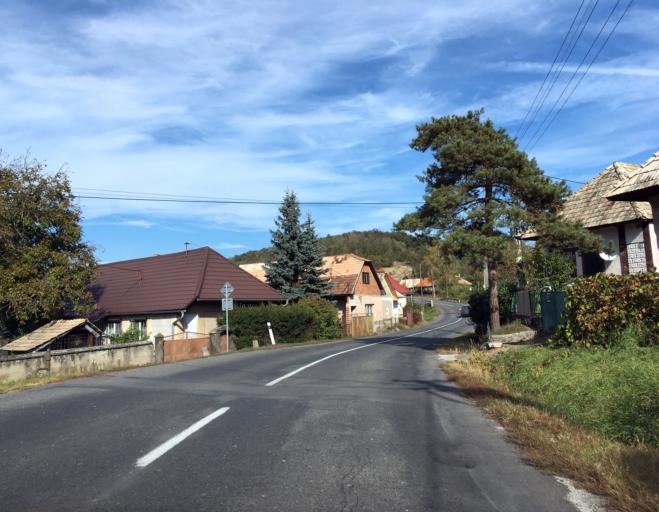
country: SK
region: Banskobystricky
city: Krupina
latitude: 48.2884
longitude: 18.9893
